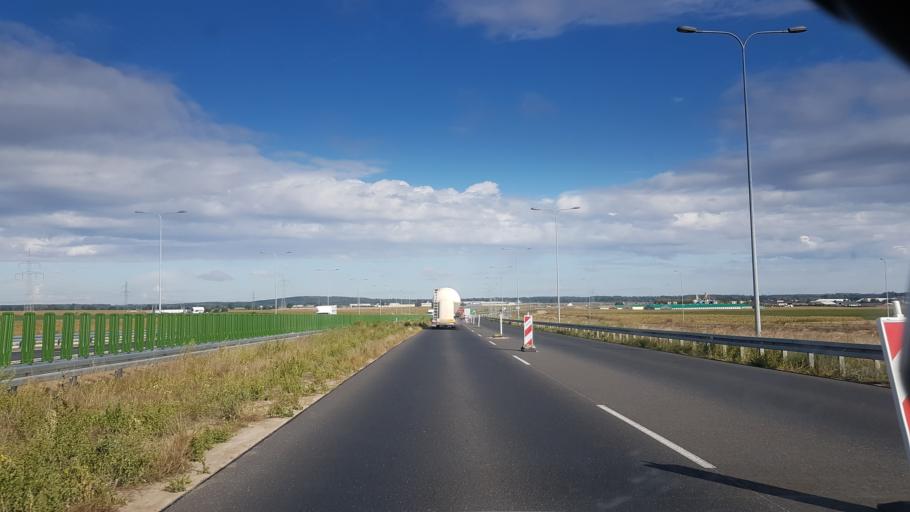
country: PL
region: Greater Poland Voivodeship
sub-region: Powiat poznanski
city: Steszew
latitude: 52.2692
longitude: 16.6678
